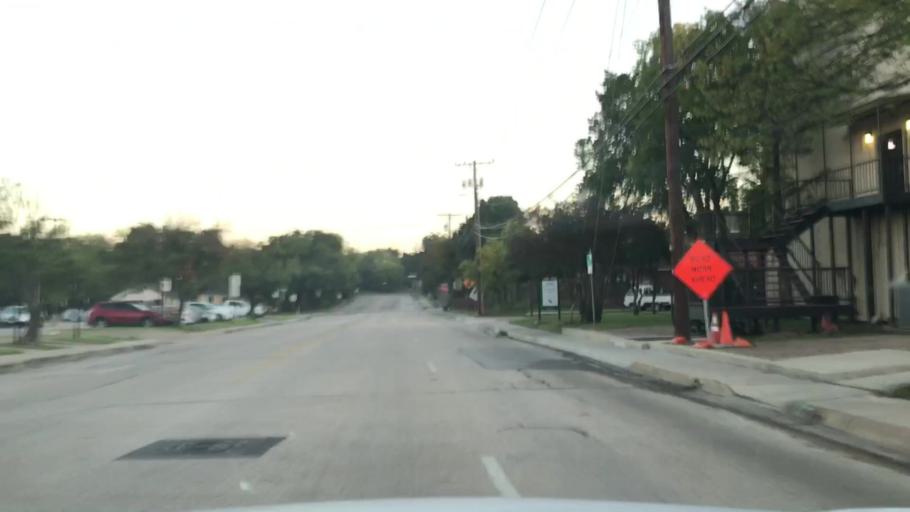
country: US
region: Texas
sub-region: Denton County
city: Denton
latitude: 33.2137
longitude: -97.1550
